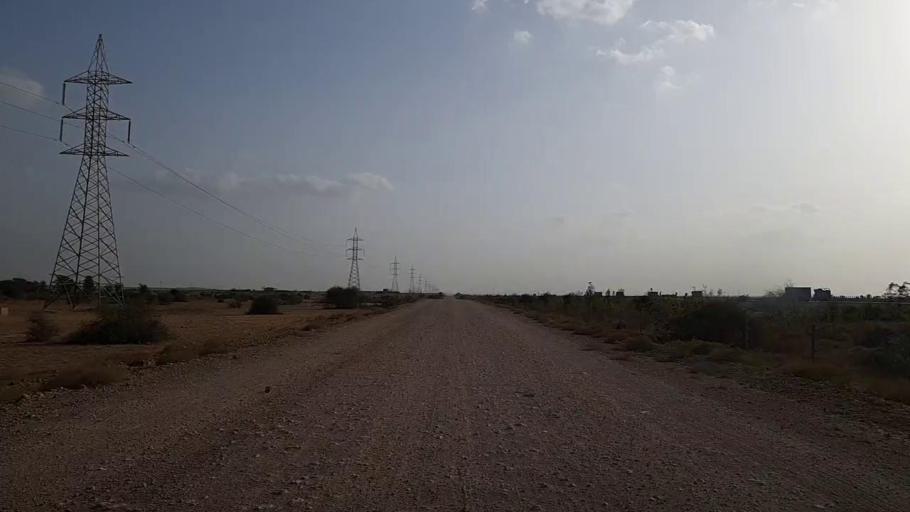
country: PK
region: Sindh
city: Kotri
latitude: 25.2108
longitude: 67.8978
